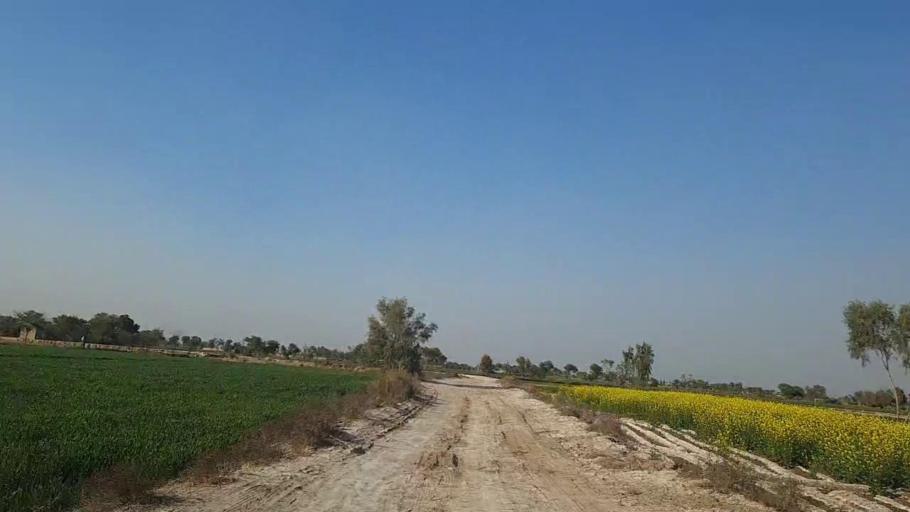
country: PK
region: Sindh
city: Daur
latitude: 26.3284
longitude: 68.1770
